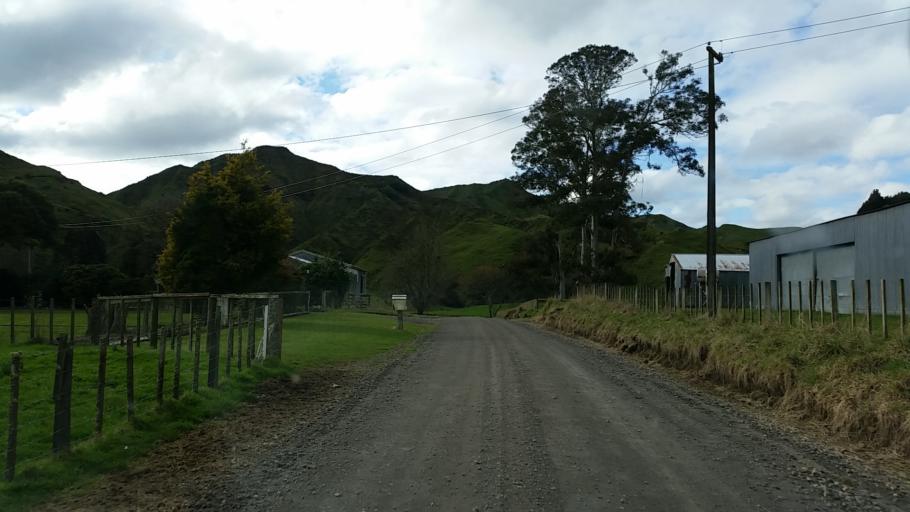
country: NZ
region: Taranaki
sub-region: New Plymouth District
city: Waitara
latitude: -39.1618
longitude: 174.5773
